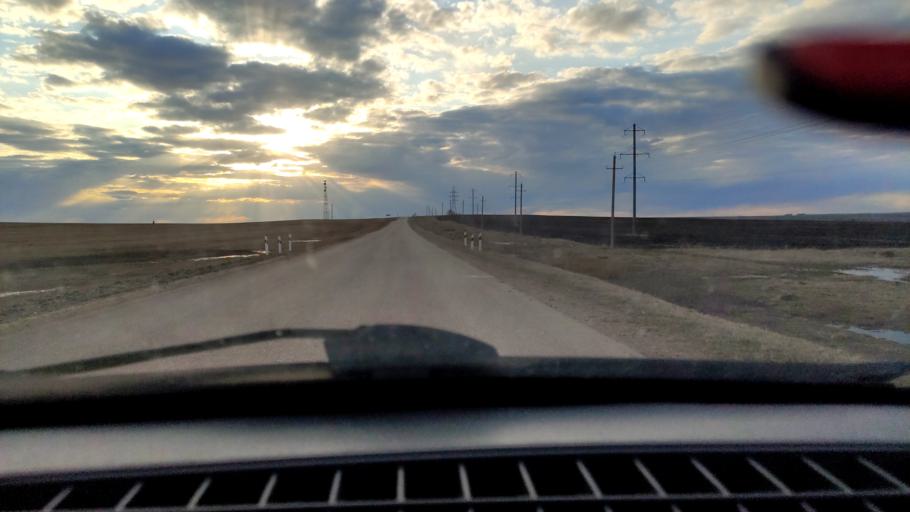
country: RU
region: Bashkortostan
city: Tolbazy
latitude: 54.0111
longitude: 55.7407
